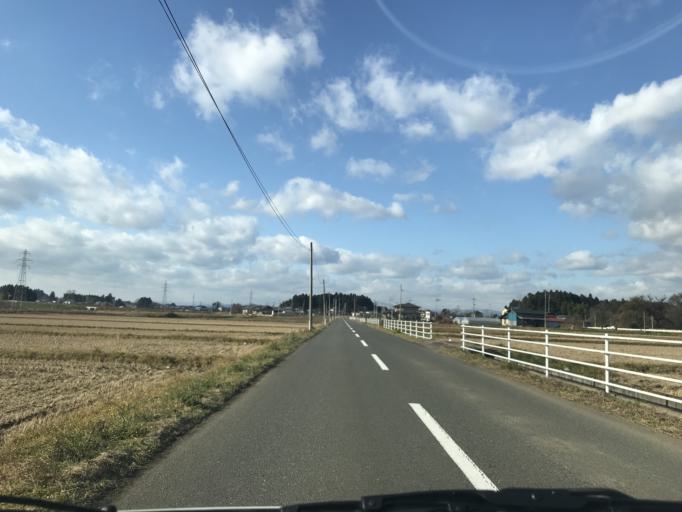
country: JP
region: Miyagi
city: Kogota
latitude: 38.7420
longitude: 141.0445
